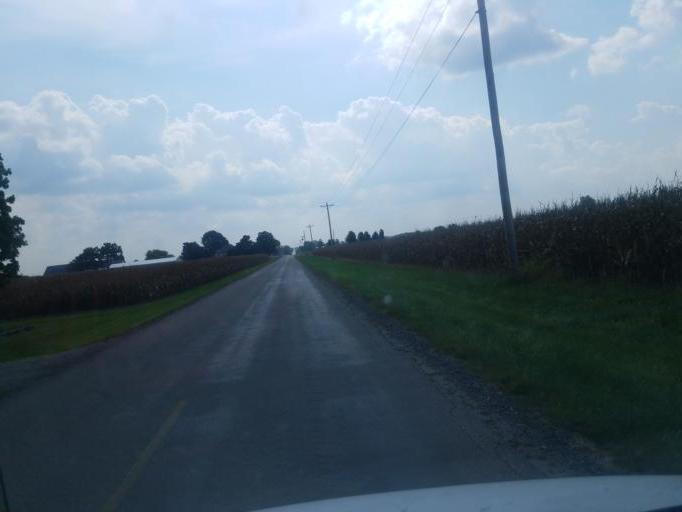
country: US
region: Ohio
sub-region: Hardin County
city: Ada
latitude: 40.6382
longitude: -83.7654
